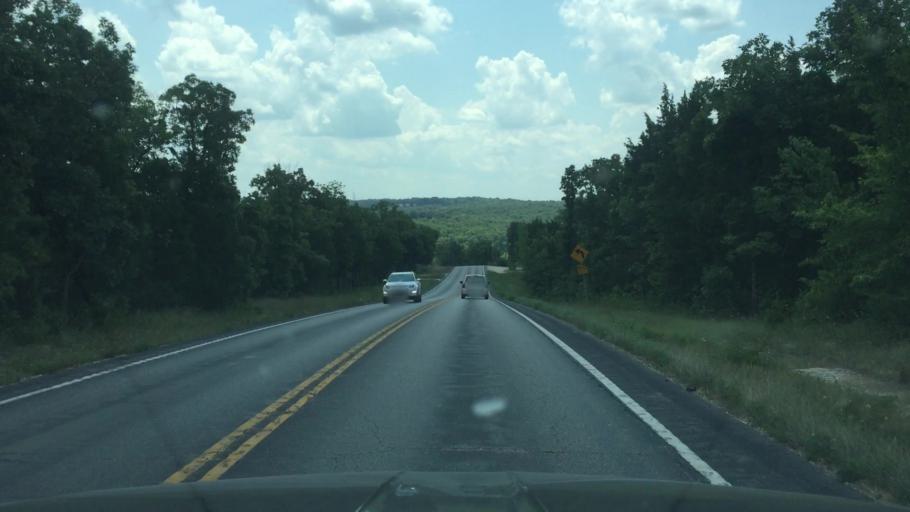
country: US
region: Missouri
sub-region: Miller County
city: Tuscumbia
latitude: 38.0907
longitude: -92.4986
